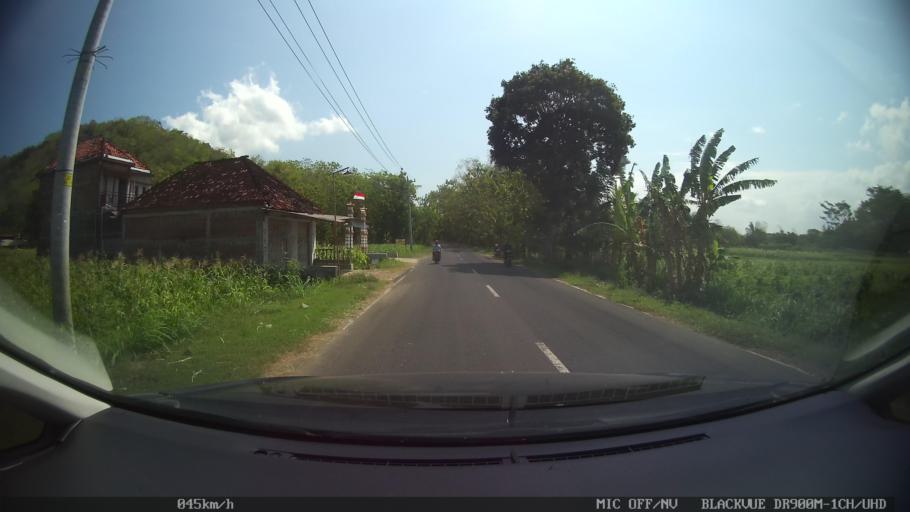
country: ID
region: Daerah Istimewa Yogyakarta
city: Pundong
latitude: -7.9566
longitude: 110.3697
